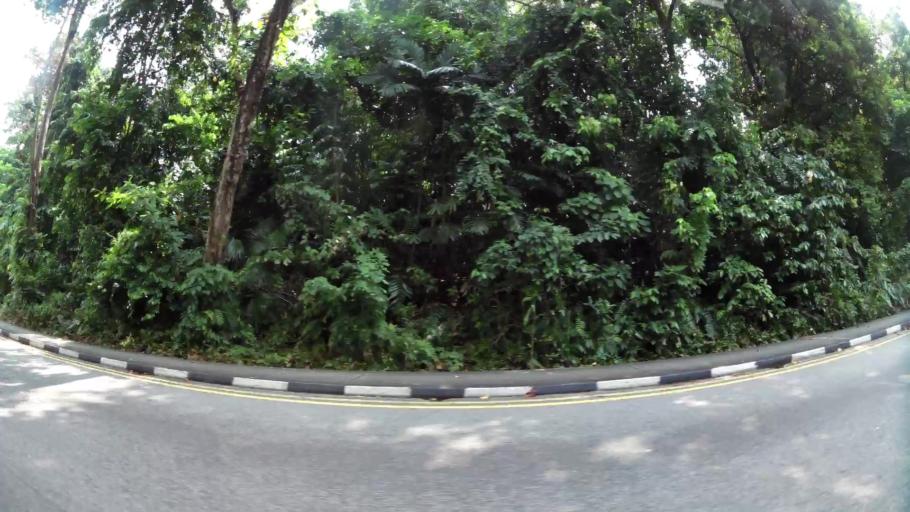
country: SG
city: Singapore
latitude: 1.3123
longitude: 103.8324
